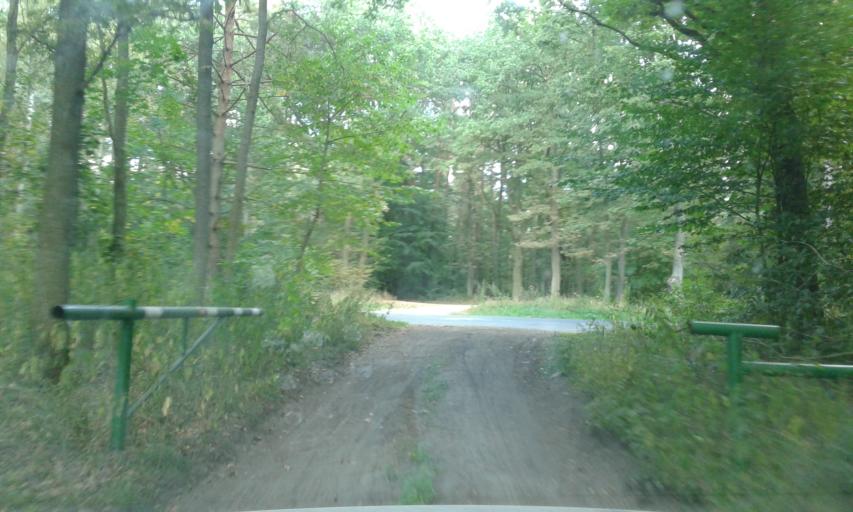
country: PL
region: West Pomeranian Voivodeship
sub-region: Powiat stargardzki
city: Dolice
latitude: 53.2305
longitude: 15.2617
